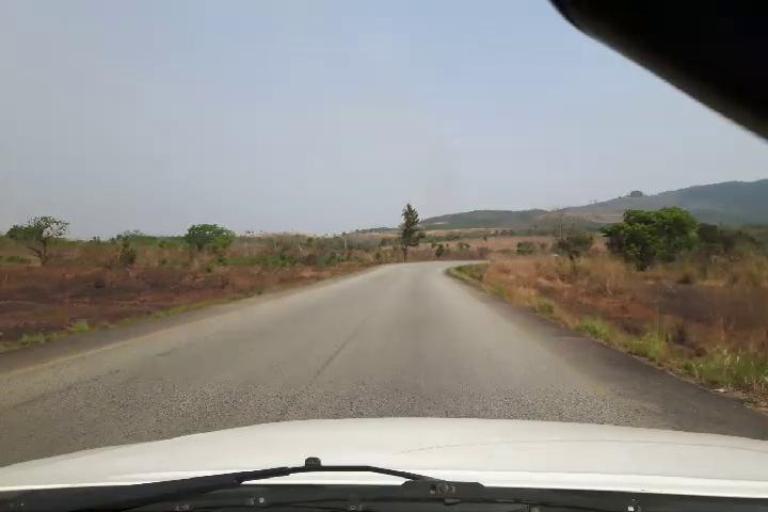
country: SL
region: Northern Province
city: Yonibana
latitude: 8.3853
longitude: -12.1934
